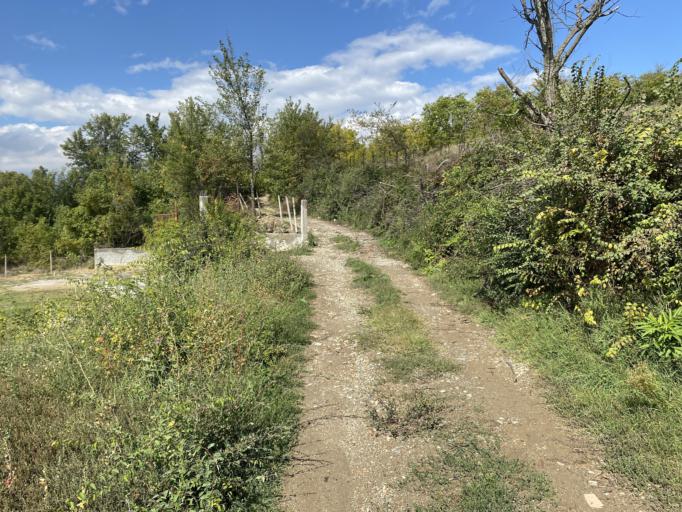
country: MK
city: Radishani
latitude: 42.0722
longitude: 21.4532
